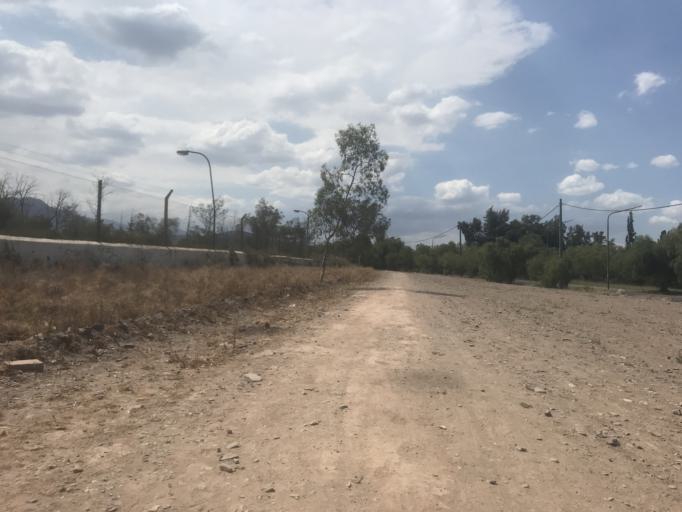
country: AR
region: Mendoza
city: Mendoza
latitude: -32.8855
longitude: -68.8850
